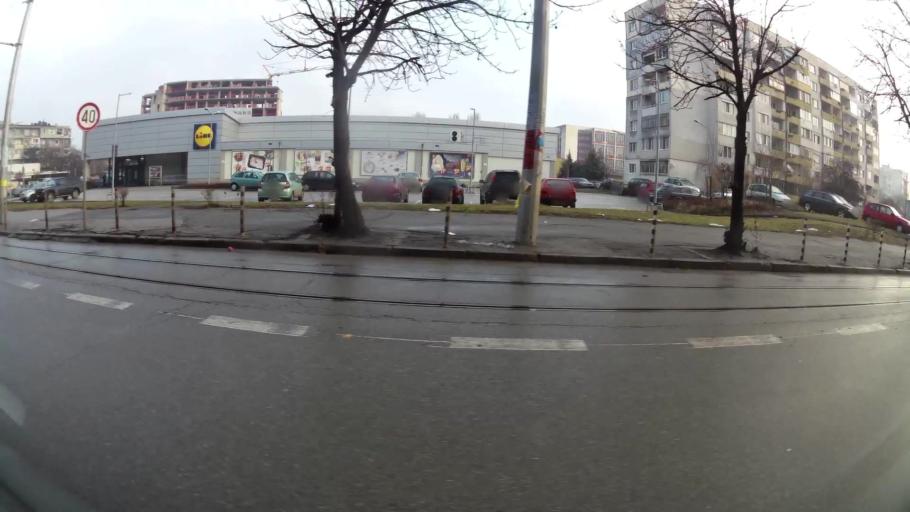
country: BG
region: Sofia-Capital
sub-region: Stolichna Obshtina
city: Sofia
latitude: 42.7334
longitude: 23.3103
